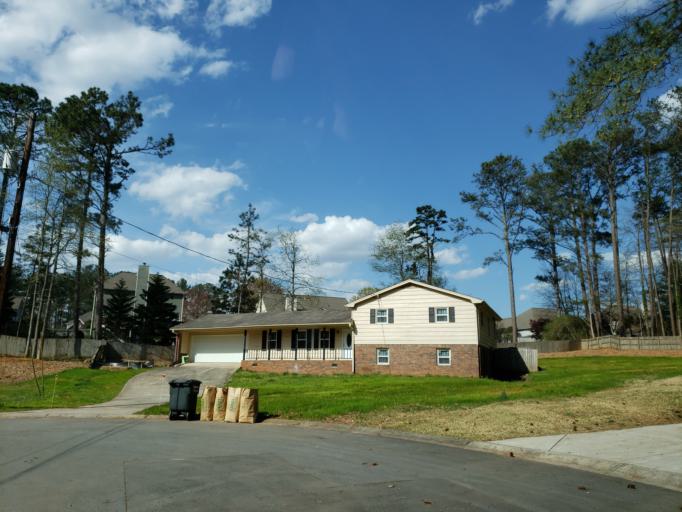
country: US
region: Georgia
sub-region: Cherokee County
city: Woodstock
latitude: 34.0355
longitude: -84.4785
